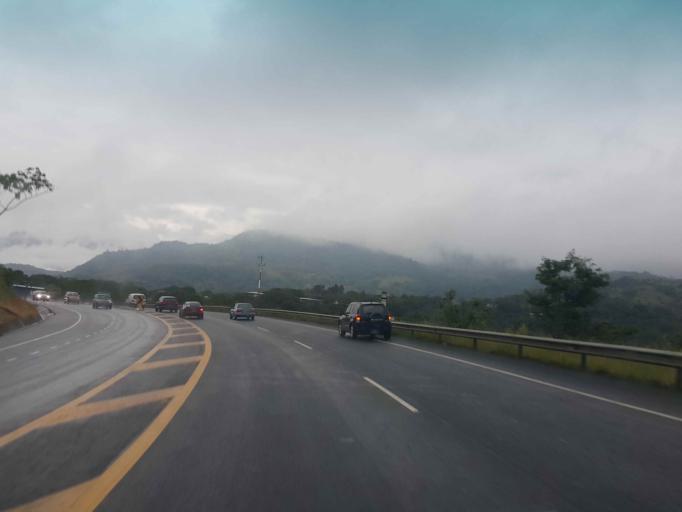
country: CR
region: Heredia
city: Colon
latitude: 9.9391
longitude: -84.2248
